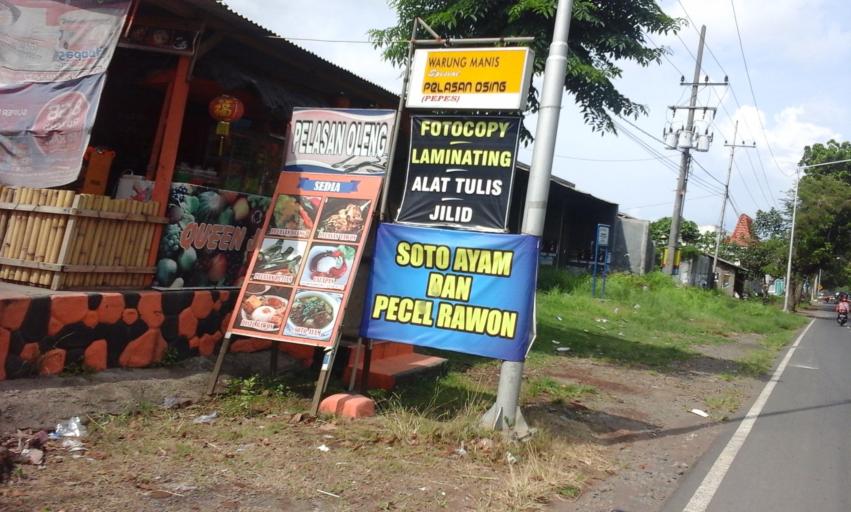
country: ID
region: East Java
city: Kepuh Wetan
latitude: -8.2520
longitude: 114.3436
